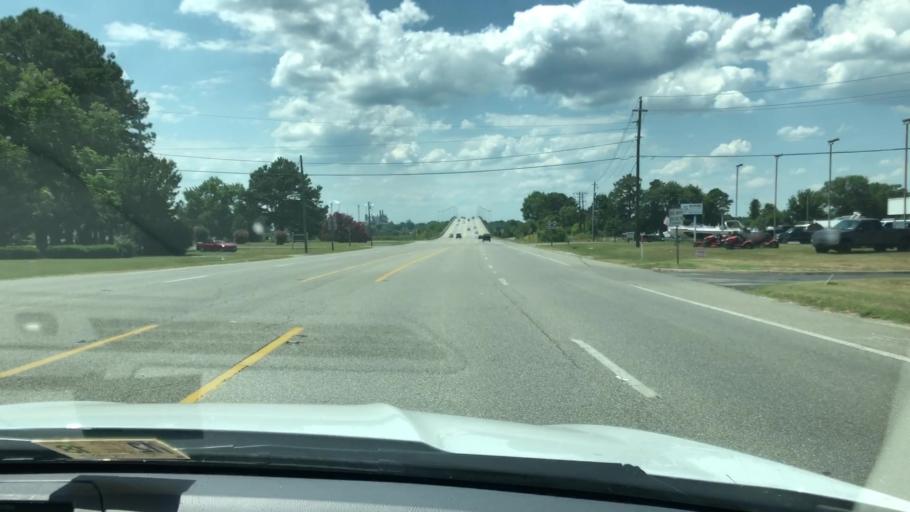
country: US
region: Virginia
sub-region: King William County
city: West Point
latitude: 37.5343
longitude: -76.7786
